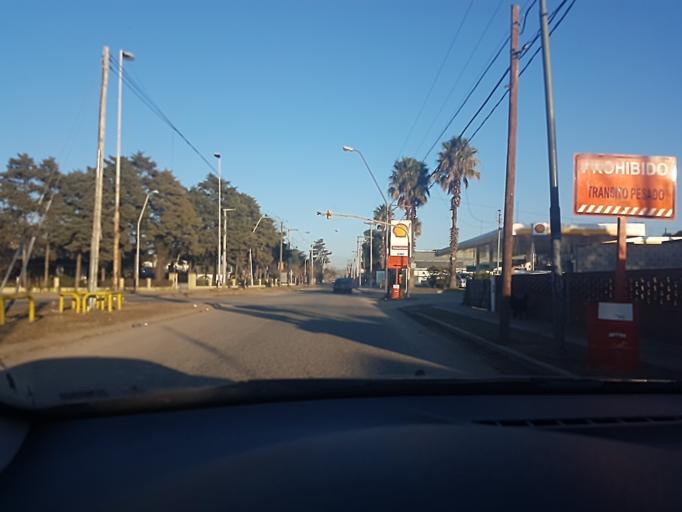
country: AR
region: Cordoba
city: Villa Allende
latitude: -31.3433
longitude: -64.2352
